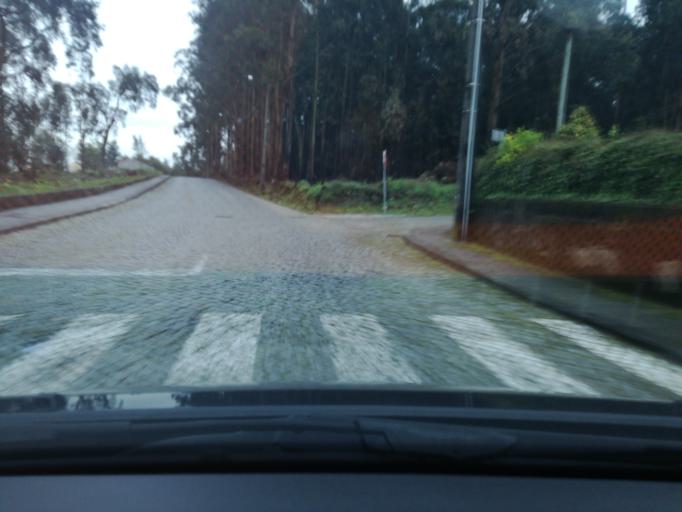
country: PT
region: Porto
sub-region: Maia
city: Gemunde
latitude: 41.2650
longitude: -8.6398
